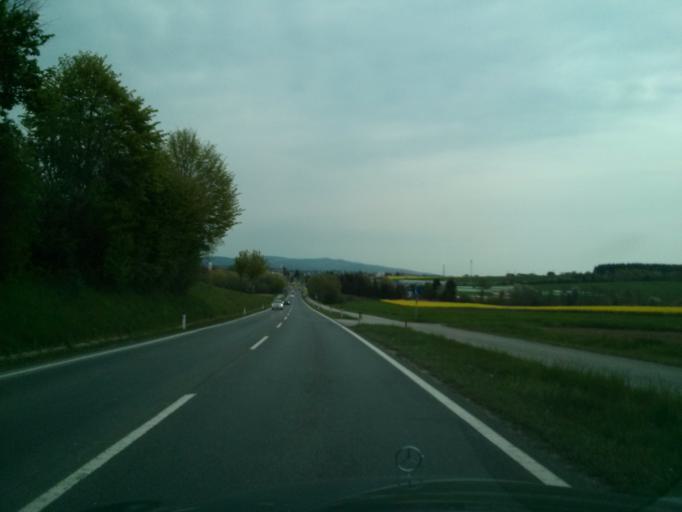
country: AT
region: Burgenland
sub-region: Politischer Bezirk Oberwart
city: Oberwart
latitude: 47.2810
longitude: 16.1790
